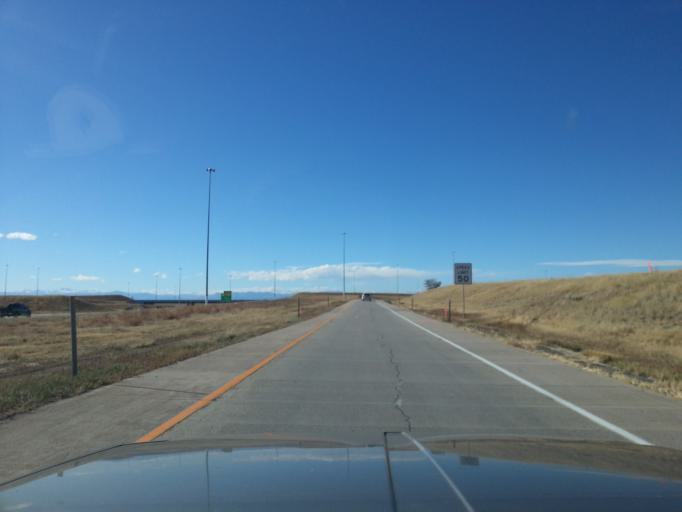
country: US
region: Colorado
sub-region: Adams County
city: Aurora
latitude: 39.8348
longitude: -104.7389
